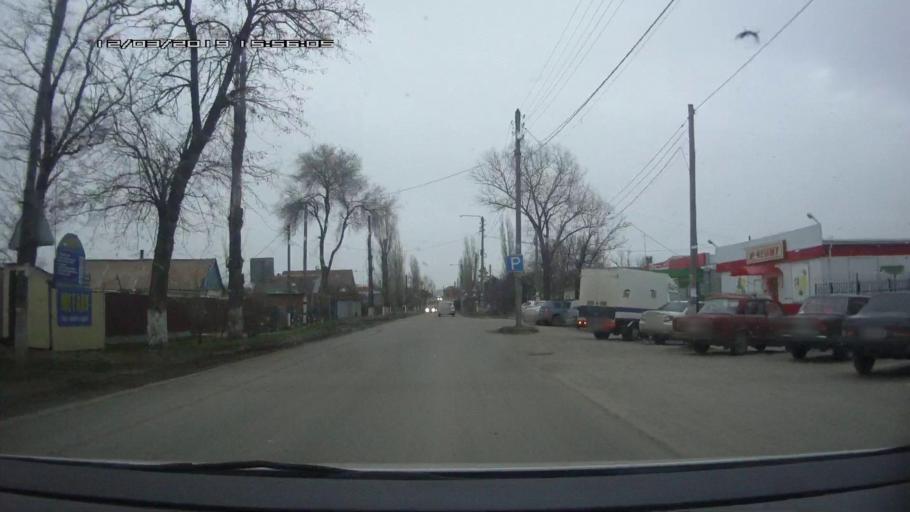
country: RU
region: Rostov
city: Novobataysk
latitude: 46.8990
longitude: 39.7807
